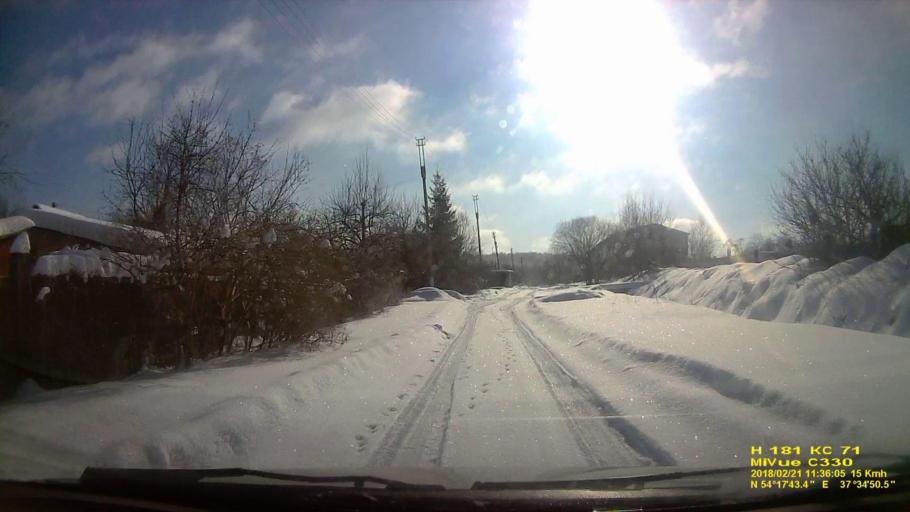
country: RU
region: Tula
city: Gorelki
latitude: 54.2953
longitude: 37.5807
